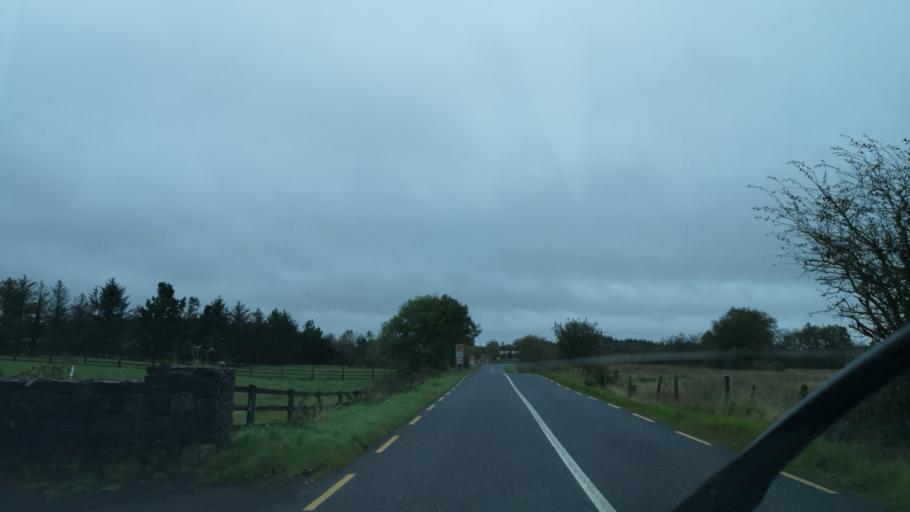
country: IE
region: Connaught
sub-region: Maigh Eo
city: Ballyhaunis
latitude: 53.7996
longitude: -8.6986
